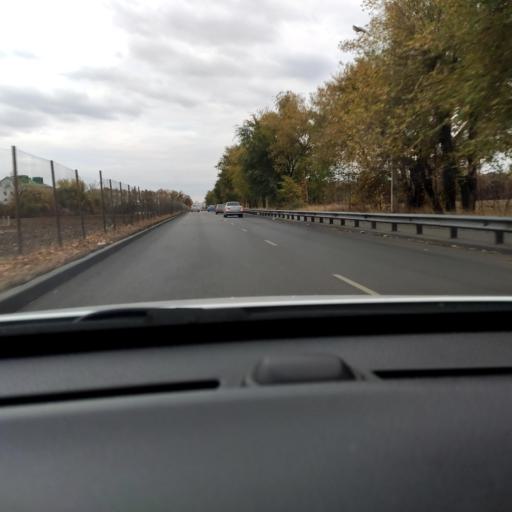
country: RU
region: Voronezj
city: Voronezh
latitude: 51.7068
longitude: 39.2259
